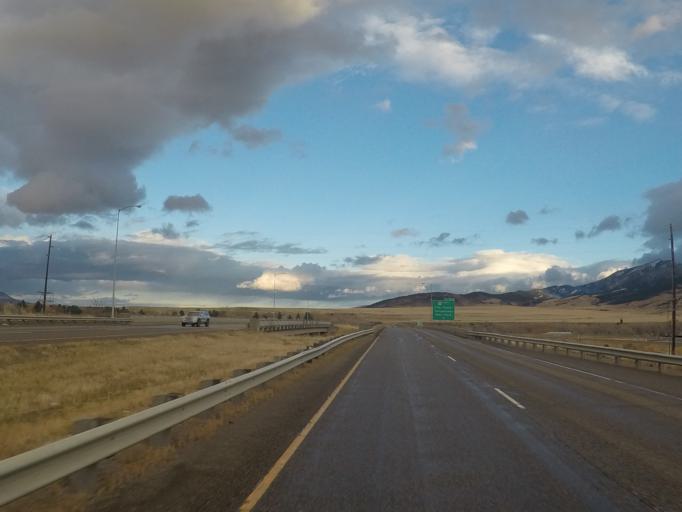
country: US
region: Montana
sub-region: Park County
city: Livingston
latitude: 45.6443
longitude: -110.5749
